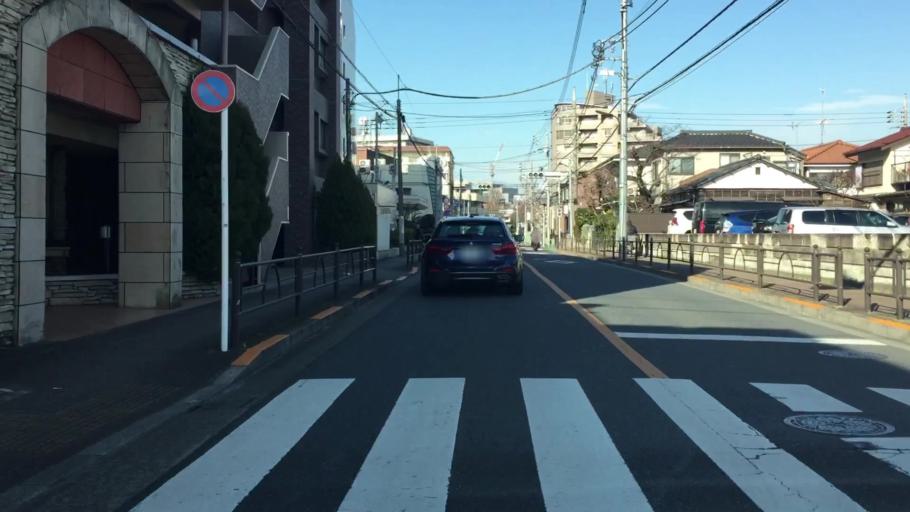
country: JP
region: Saitama
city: Wako
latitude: 35.7574
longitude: 139.6623
